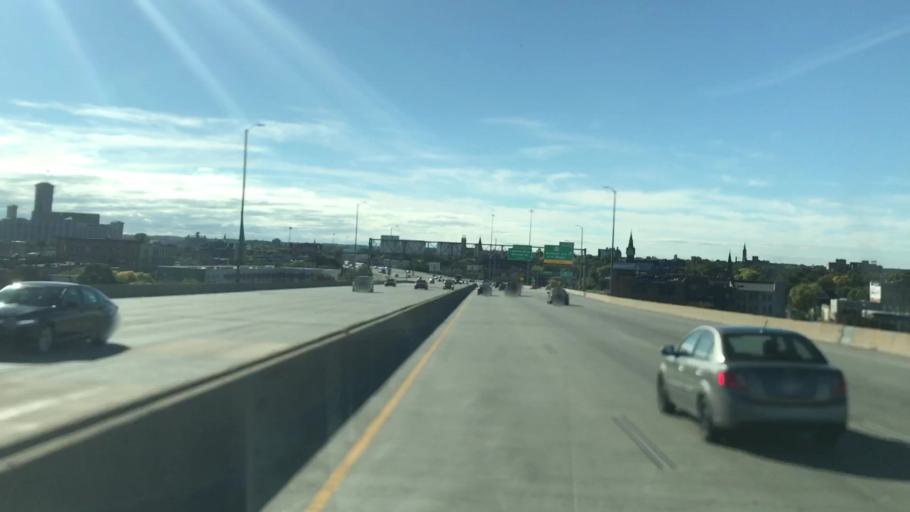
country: US
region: Wisconsin
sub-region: Milwaukee County
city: Milwaukee
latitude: 43.0263
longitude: -87.9220
